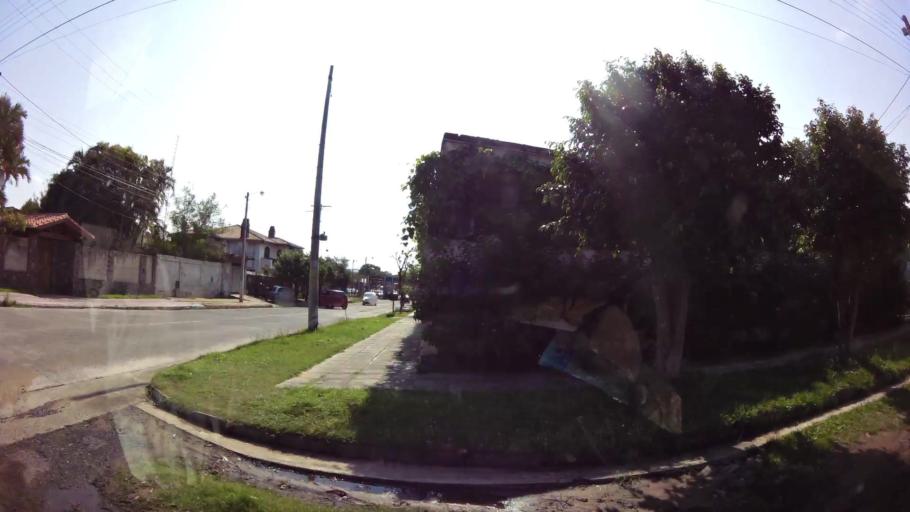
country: PY
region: Asuncion
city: Asuncion
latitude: -25.3245
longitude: -57.6346
